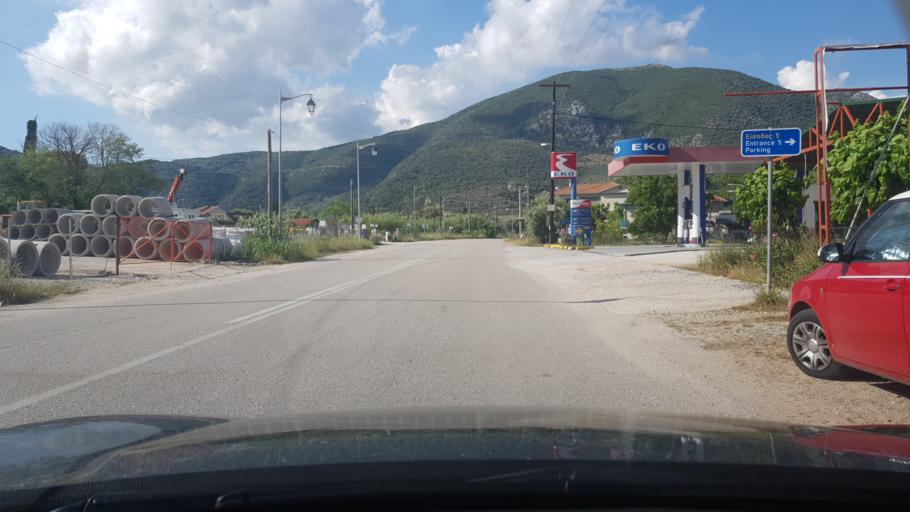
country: GR
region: Ionian Islands
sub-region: Lefkada
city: Nidri
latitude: 38.7049
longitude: 20.7038
